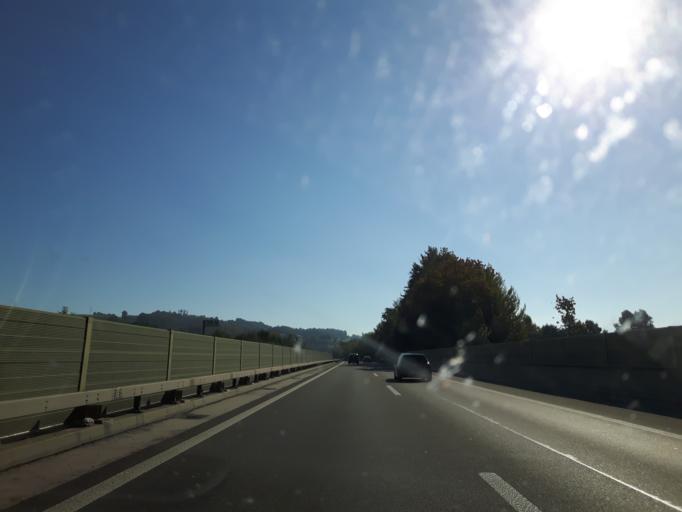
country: CH
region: Lucerne
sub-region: Sursee District
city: Sursee
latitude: 47.1743
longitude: 8.1277
